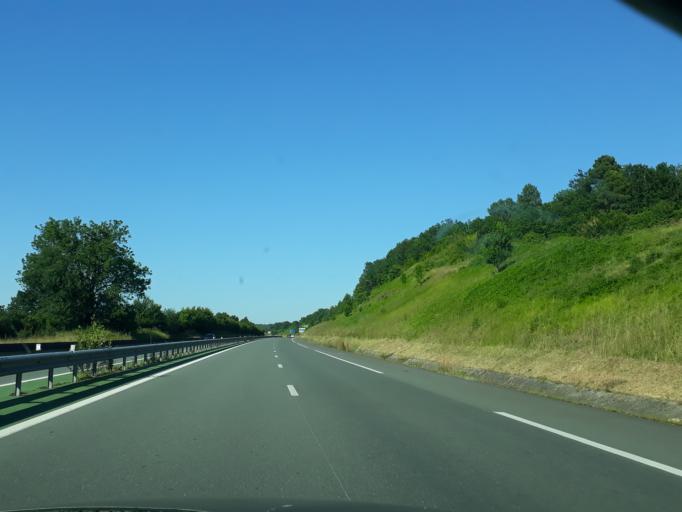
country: FR
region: Aquitaine
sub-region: Departement de la Dordogne
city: Neuvic
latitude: 45.0709
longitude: 0.4393
